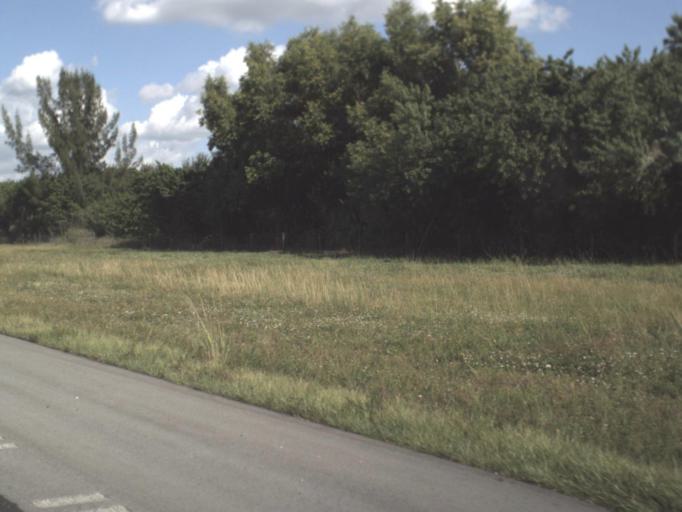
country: US
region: Florida
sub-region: Palm Beach County
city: Villages of Oriole
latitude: 26.4366
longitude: -80.1737
